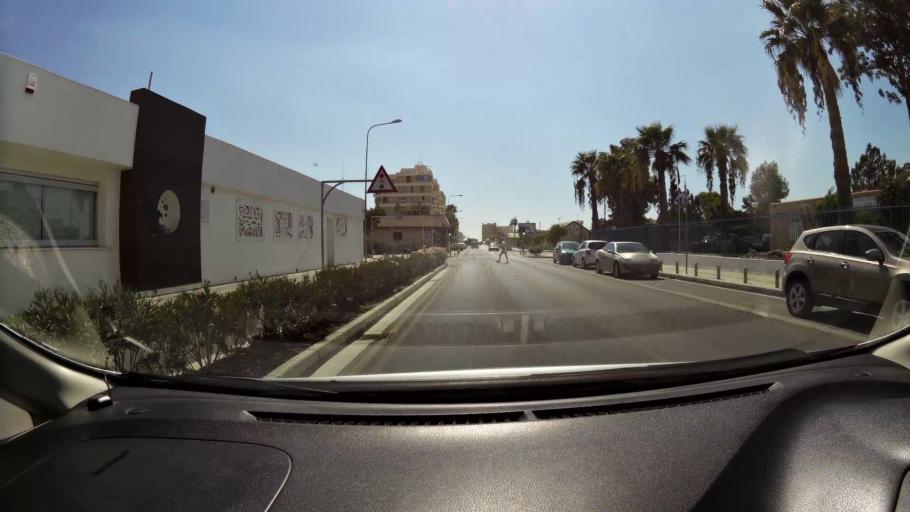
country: CY
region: Larnaka
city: Larnaca
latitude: 34.8996
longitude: 33.6381
